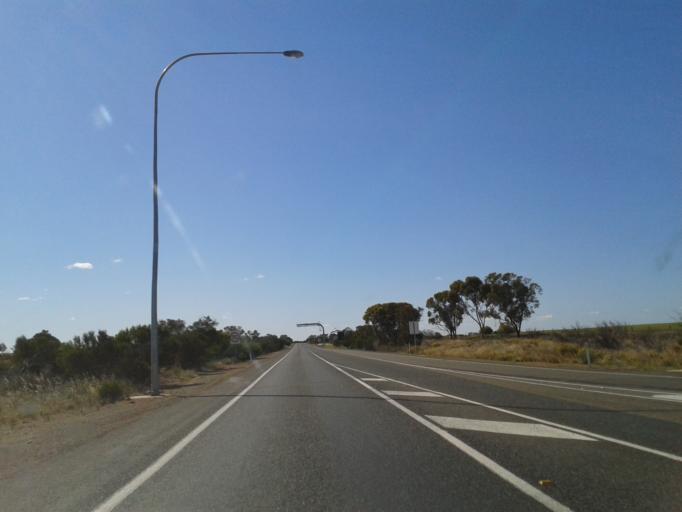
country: AU
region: South Australia
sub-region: Renmark Paringa
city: Renmark
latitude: -34.2618
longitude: 140.8669
